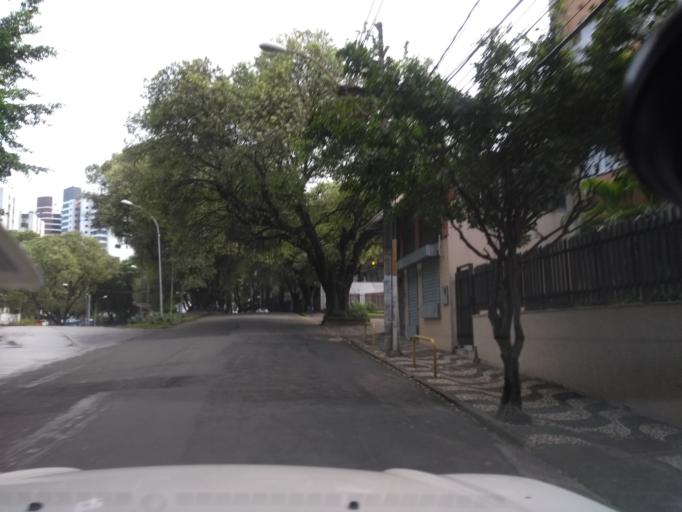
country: BR
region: Bahia
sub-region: Salvador
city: Salvador
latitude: -13.0006
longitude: -38.5239
